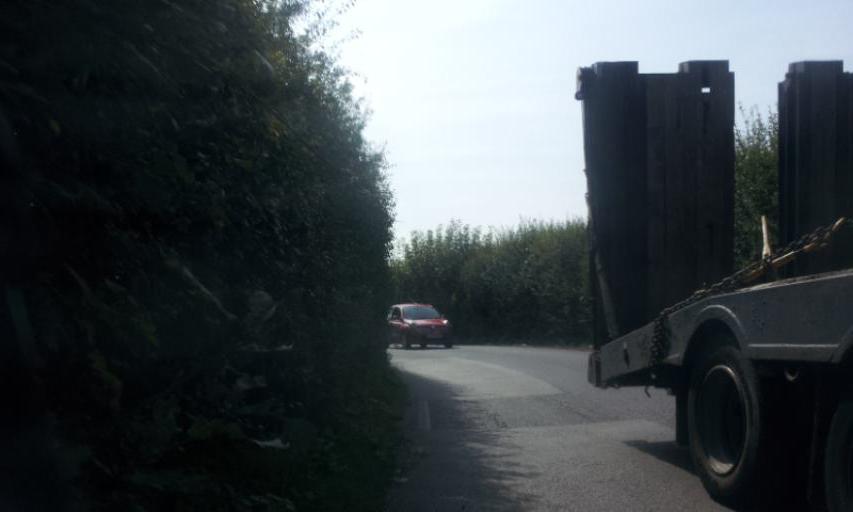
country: GB
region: England
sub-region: Kent
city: Paddock Wood
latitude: 51.1709
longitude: 0.4022
